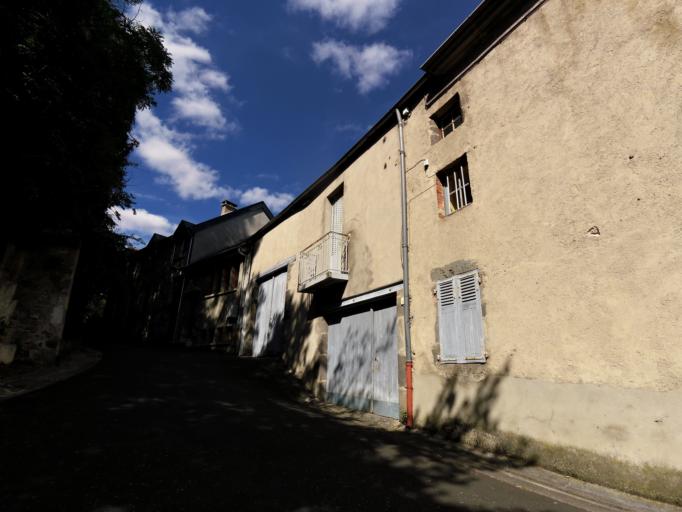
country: FR
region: Auvergne
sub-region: Departement du Puy-de-Dome
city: Aydat
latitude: 45.5879
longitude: 2.9930
